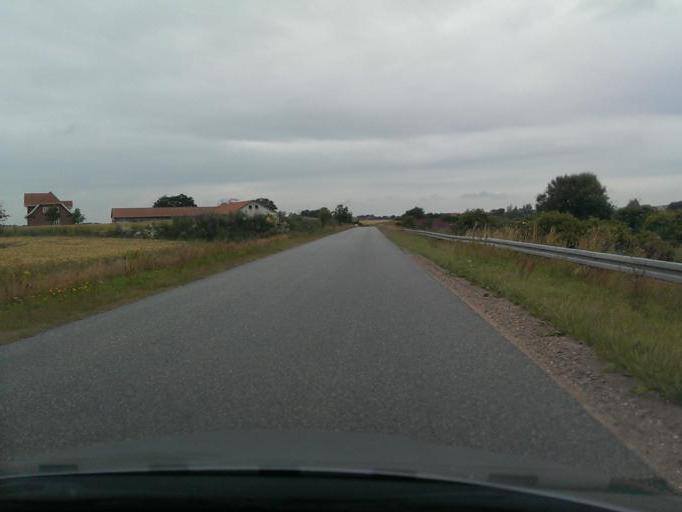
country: DK
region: North Denmark
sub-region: Hjorring Kommune
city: Vra
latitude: 57.3547
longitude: 9.9303
